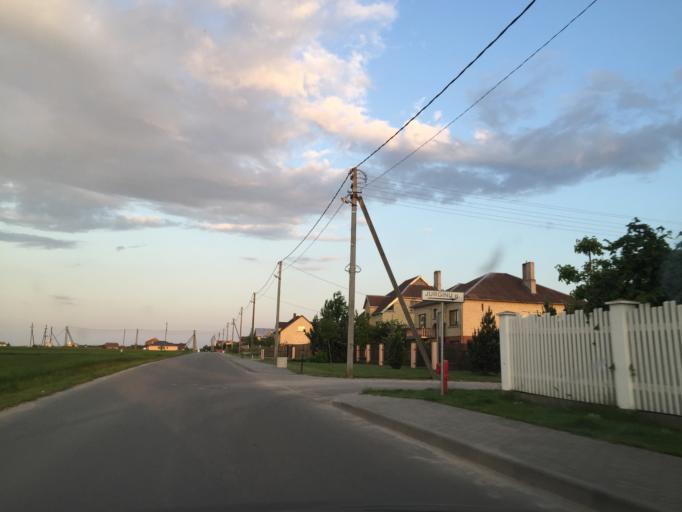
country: LT
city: Kursenai
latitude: 56.0128
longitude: 22.9486
